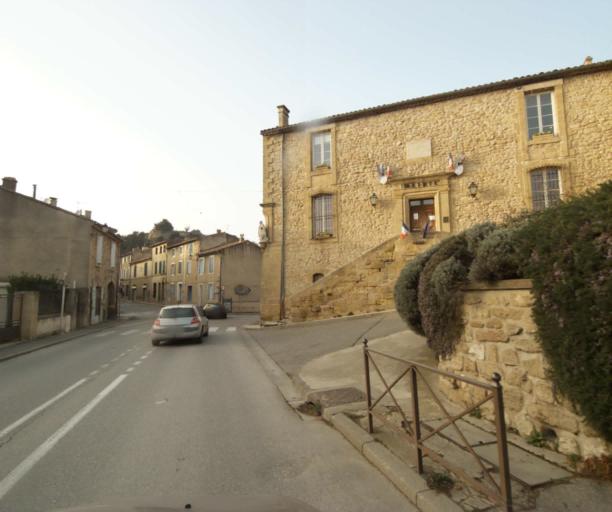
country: FR
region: Provence-Alpes-Cote d'Azur
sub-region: Departement des Bouches-du-Rhone
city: Rognes
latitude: 43.6630
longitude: 5.3491
